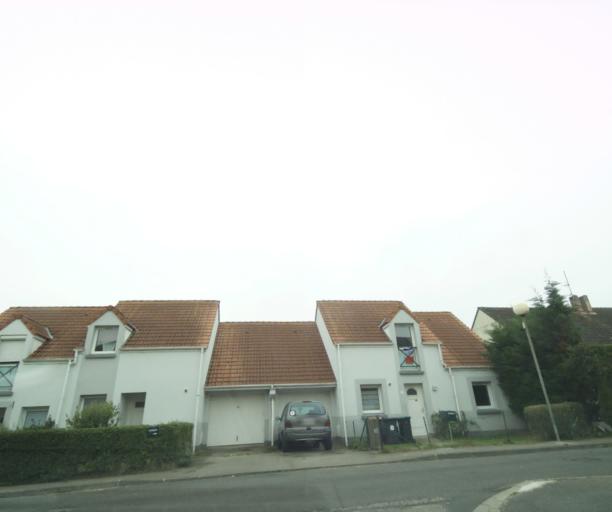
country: FR
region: Nord-Pas-de-Calais
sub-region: Departement du Pas-de-Calais
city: Etaples
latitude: 50.5175
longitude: 1.6471
